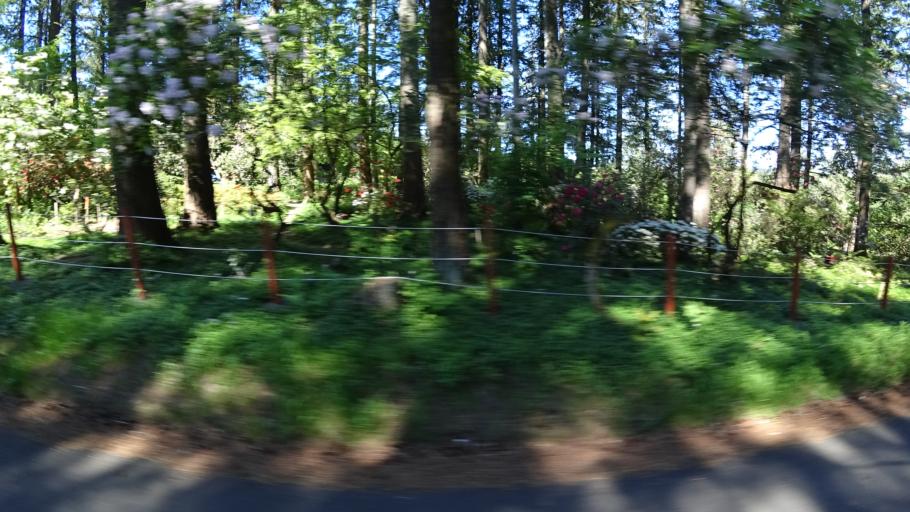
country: US
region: Oregon
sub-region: Washington County
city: Oak Hills
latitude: 45.5561
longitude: -122.8186
